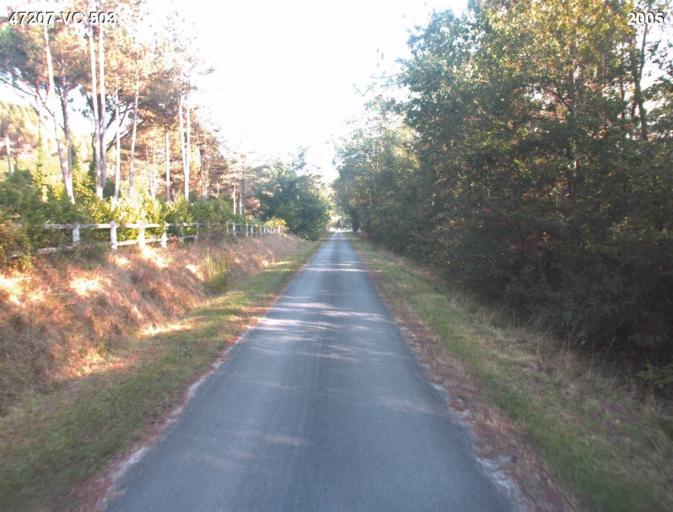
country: FR
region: Aquitaine
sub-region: Departement du Lot-et-Garonne
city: Barbaste
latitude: 44.1901
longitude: 0.2312
